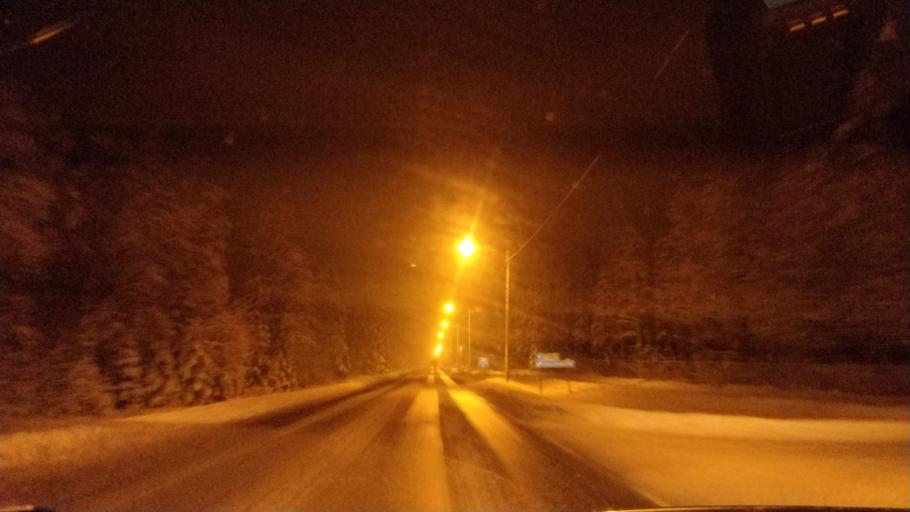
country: FI
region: Lapland
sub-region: Rovaniemi
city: Rovaniemi
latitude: 66.4218
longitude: 25.4190
